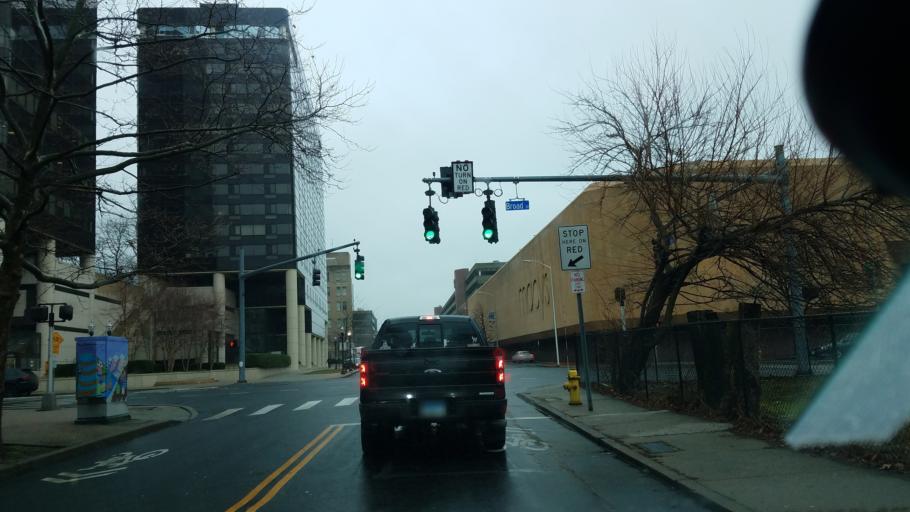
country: US
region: Connecticut
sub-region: Fairfield County
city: Stamford
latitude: 41.0555
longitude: -73.5361
